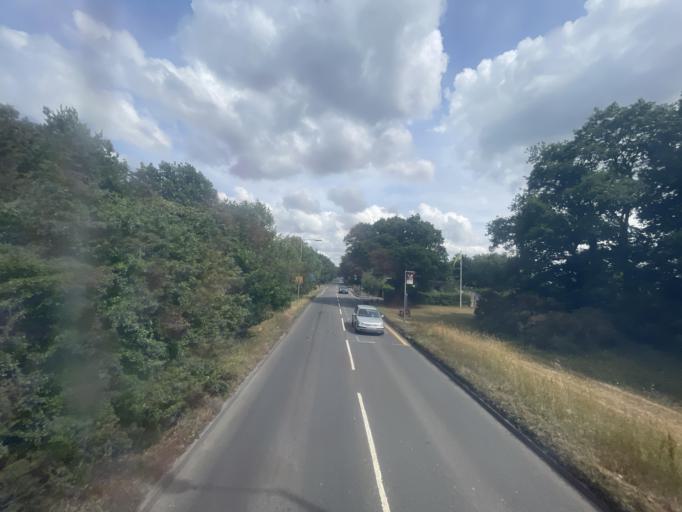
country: GB
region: England
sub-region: Greater London
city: West Wickham
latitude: 51.3687
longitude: 0.0125
